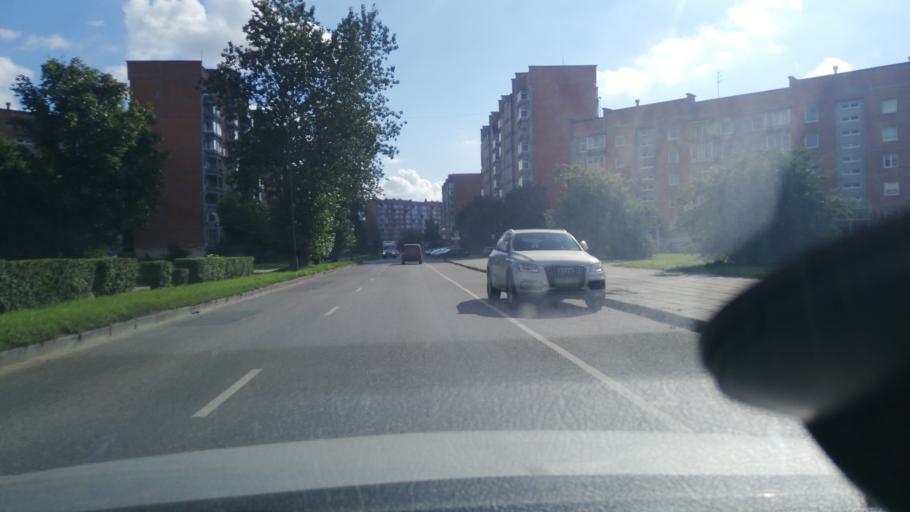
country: LT
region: Klaipedos apskritis
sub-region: Klaipeda
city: Klaipeda
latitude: 55.6701
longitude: 21.1996
